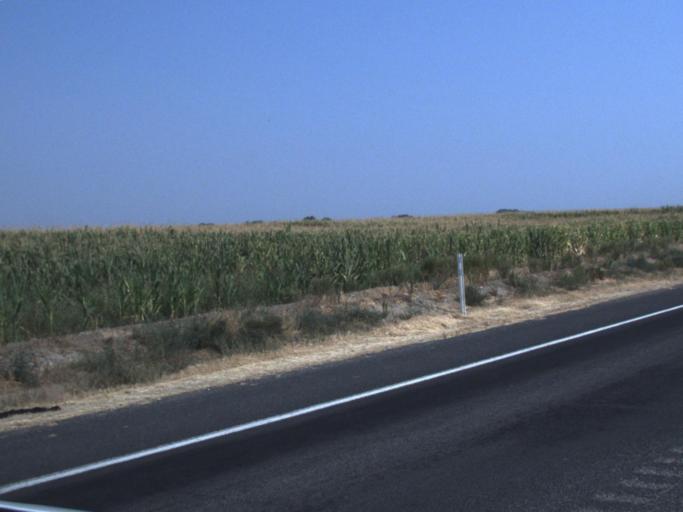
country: US
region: Washington
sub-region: Yakima County
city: Toppenish
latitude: 46.3664
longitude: -120.3124
